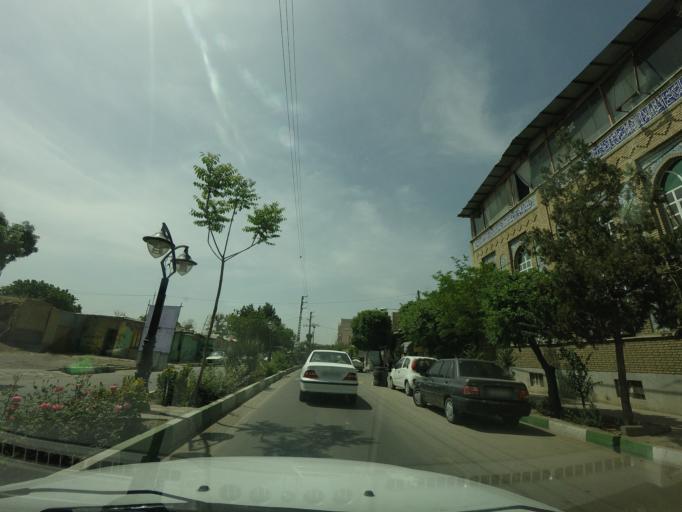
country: IR
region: Tehran
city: Eslamshahr
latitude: 35.6283
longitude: 51.2512
